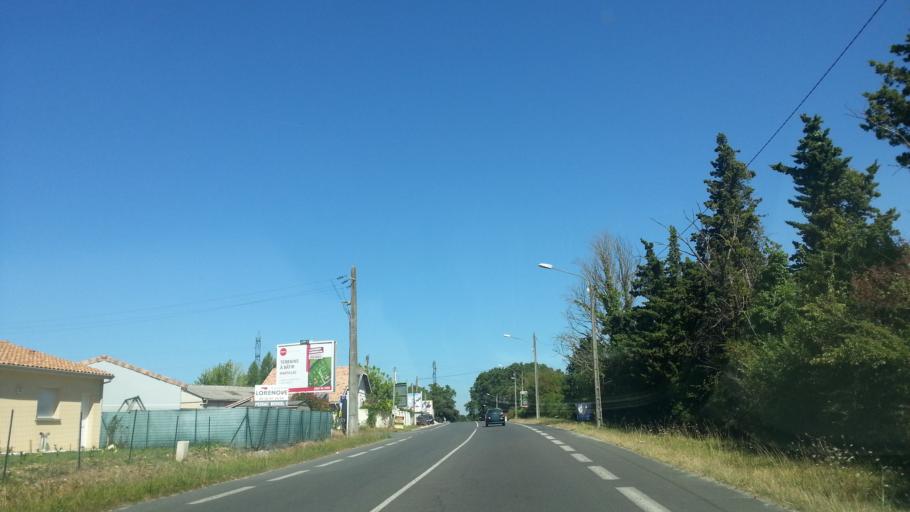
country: FR
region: Aquitaine
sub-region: Departement de la Gironde
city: Cadaujac
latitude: 44.7546
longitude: -0.5510
